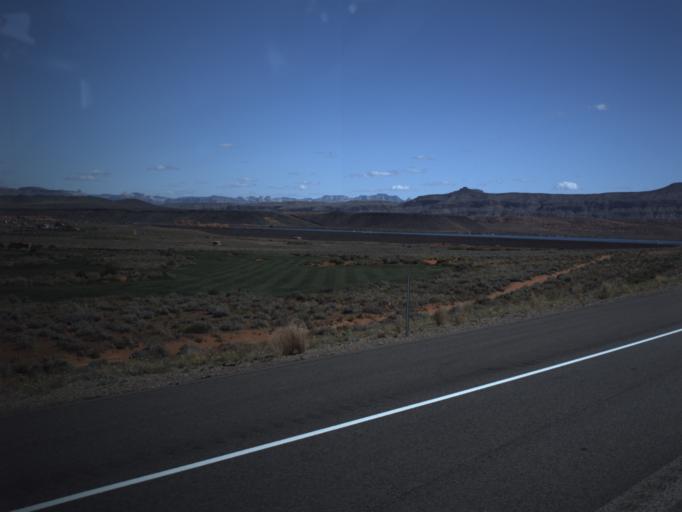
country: US
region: Utah
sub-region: Washington County
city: Washington
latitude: 37.1085
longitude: -113.4048
